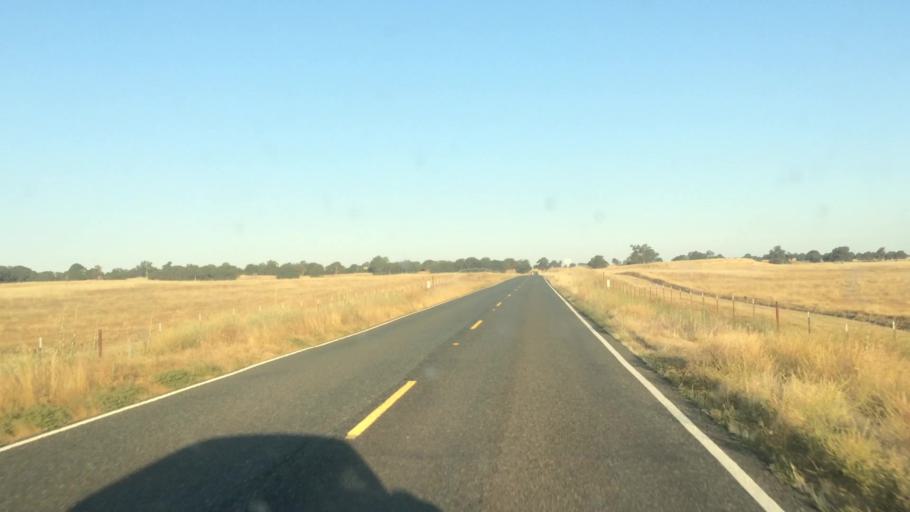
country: US
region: California
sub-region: Amador County
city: Ione
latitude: 38.3644
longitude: -121.0283
